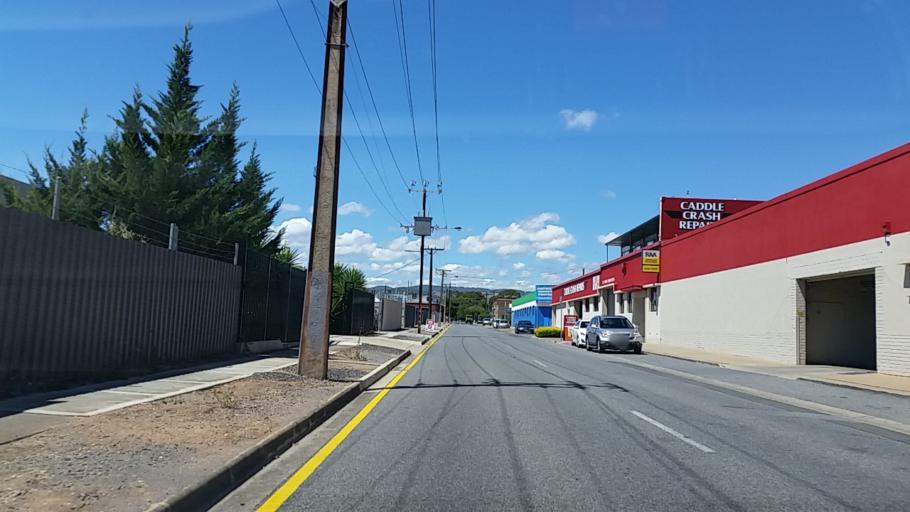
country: AU
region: South Australia
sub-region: Marion
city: Clovelly Park
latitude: -34.9866
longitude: 138.5707
